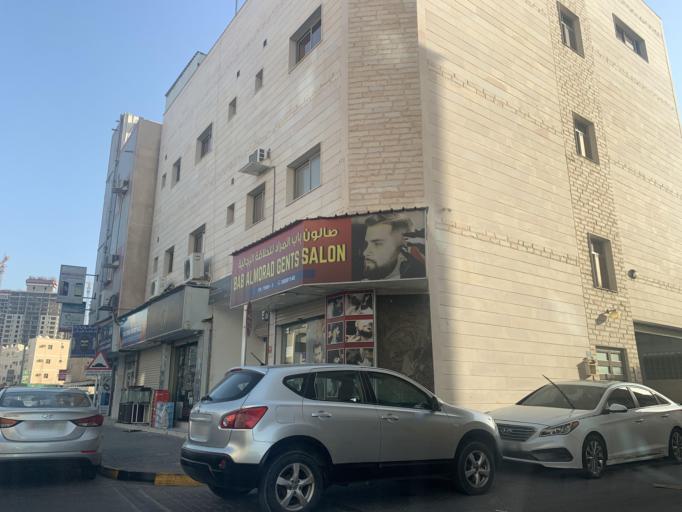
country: BH
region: Manama
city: Jidd Hafs
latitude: 26.2084
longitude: 50.4520
